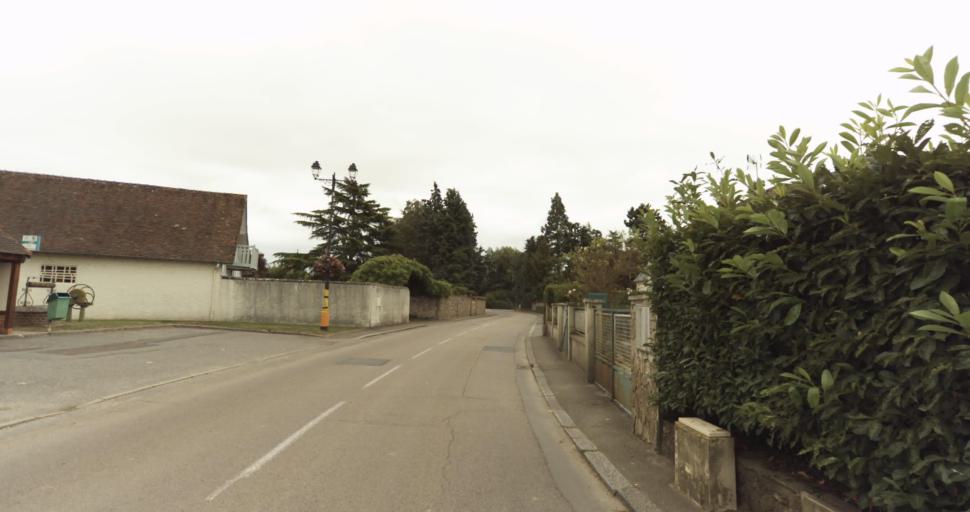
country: FR
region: Haute-Normandie
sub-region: Departement de l'Eure
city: Gravigny
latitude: 49.0382
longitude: 1.2076
